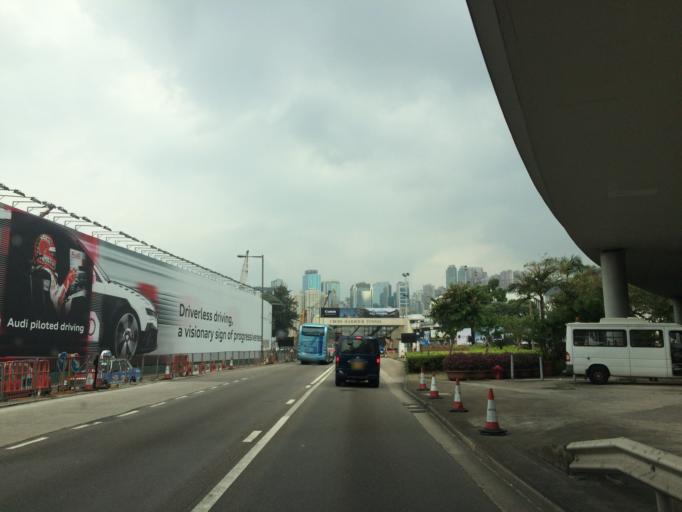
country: HK
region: Wanchai
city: Wan Chai
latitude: 22.2823
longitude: 114.1807
